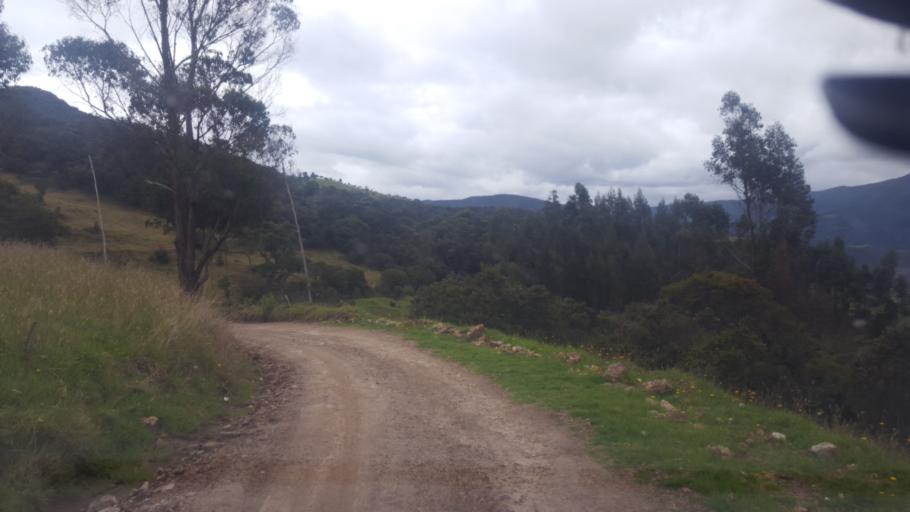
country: CO
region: Boyaca
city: Belen
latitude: 6.0281
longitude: -72.8817
